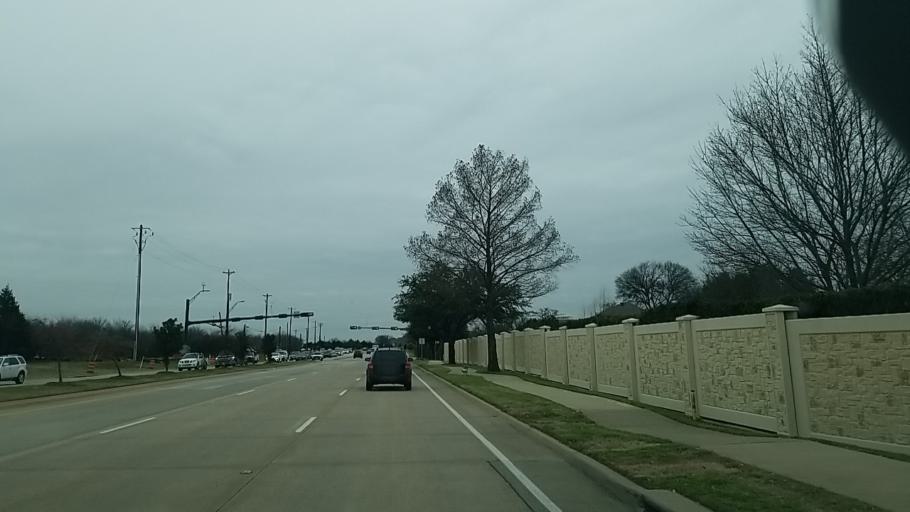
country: US
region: Texas
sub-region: Denton County
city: Flower Mound
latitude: 33.0041
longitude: -97.0708
